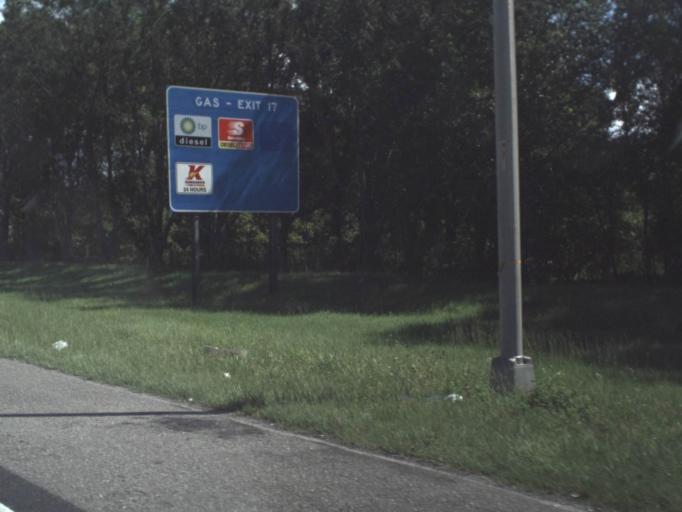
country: US
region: Florida
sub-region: Clay County
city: Bellair-Meadowbrook Terrace
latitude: 30.2634
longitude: -81.7646
